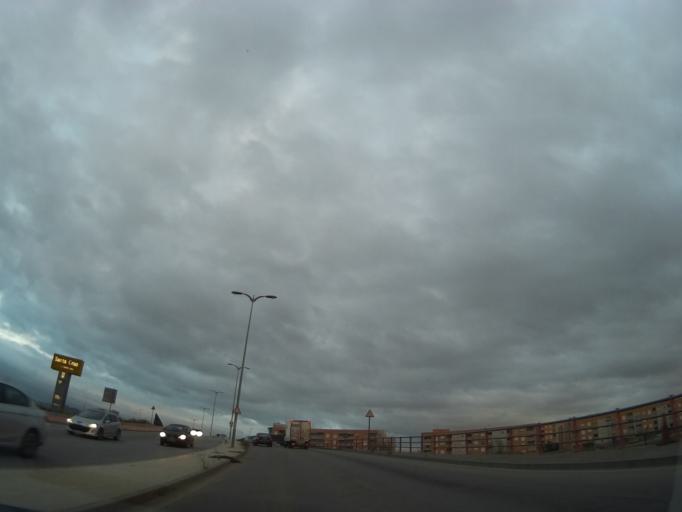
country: ES
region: Andalusia
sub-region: Provincia de Malaga
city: Malaga
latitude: 36.7017
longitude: -4.4920
